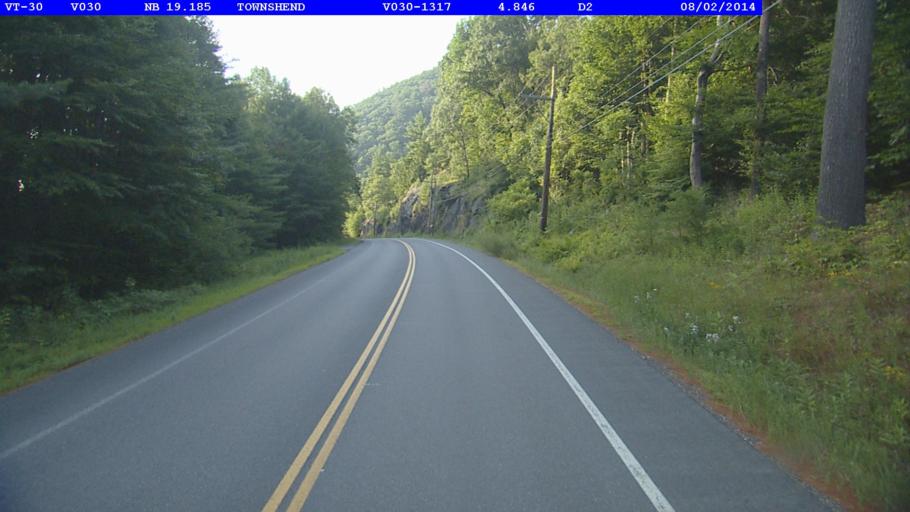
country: US
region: Vermont
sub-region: Windham County
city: Newfane
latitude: 43.0642
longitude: -72.6977
